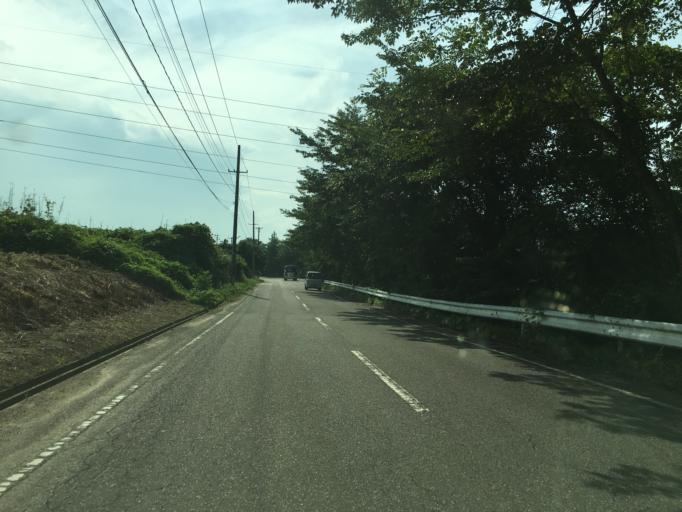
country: JP
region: Fukushima
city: Sukagawa
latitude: 37.3315
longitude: 140.4260
